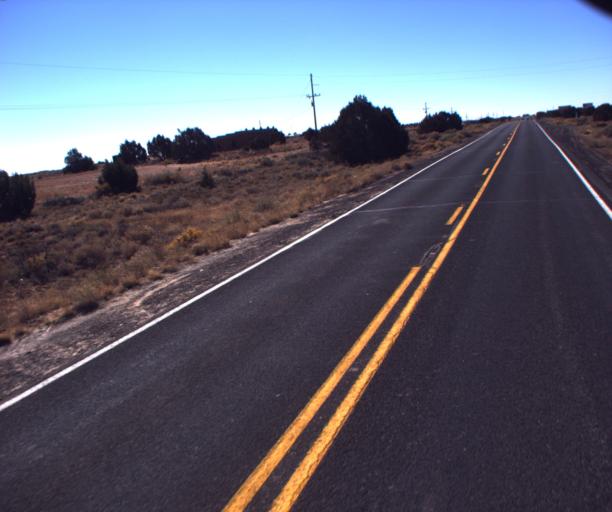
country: US
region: Arizona
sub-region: Navajo County
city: First Mesa
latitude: 35.8353
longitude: -110.5282
